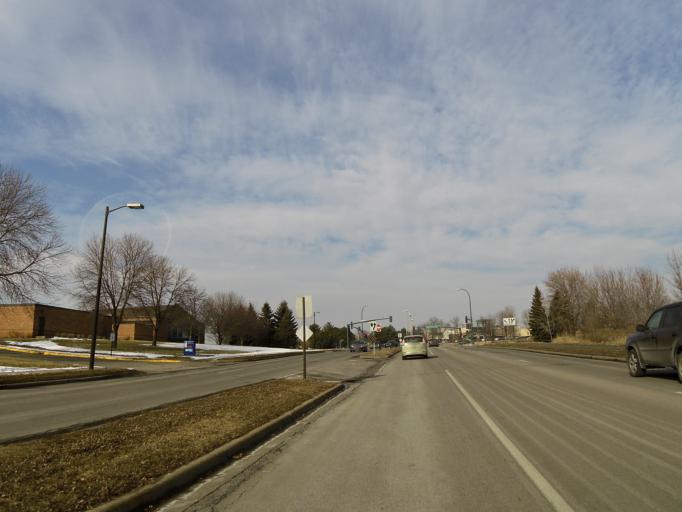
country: US
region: Minnesota
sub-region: Hennepin County
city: Eden Prairie
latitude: 44.8500
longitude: -93.4240
